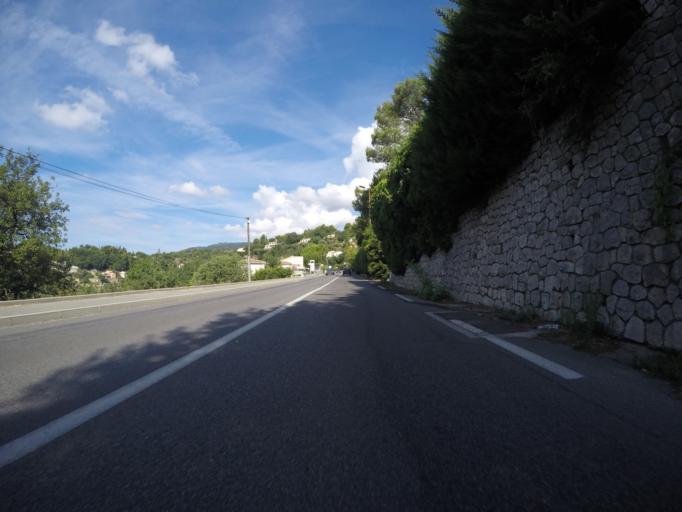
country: FR
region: Provence-Alpes-Cote d'Azur
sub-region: Departement des Alpes-Maritimes
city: Opio
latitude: 43.6770
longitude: 6.9814
